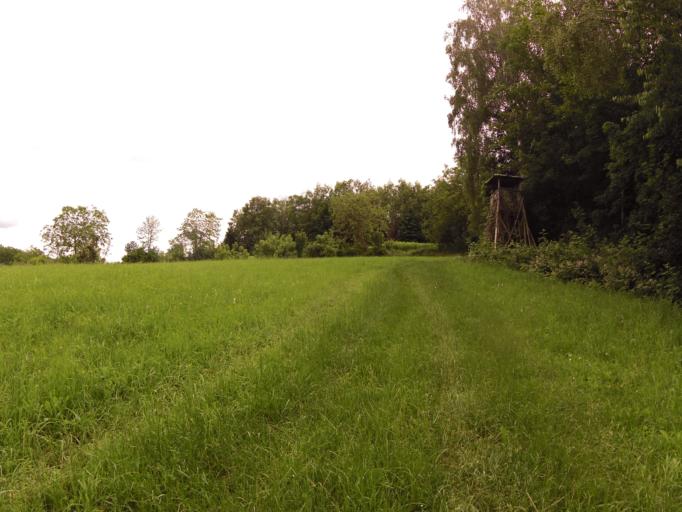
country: DE
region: Baden-Wuerttemberg
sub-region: Freiburg Region
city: Lahr
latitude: 48.3534
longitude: 7.8608
